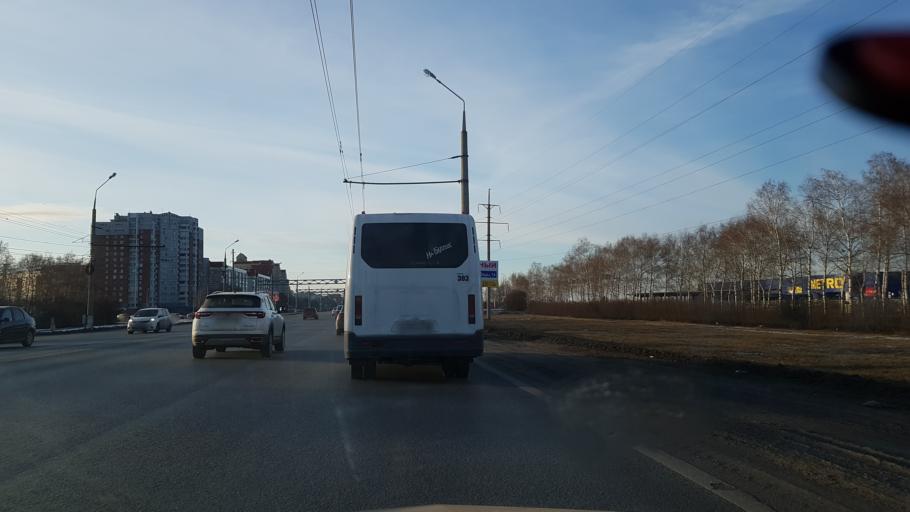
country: RU
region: Samara
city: Tol'yatti
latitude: 53.5456
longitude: 49.3770
